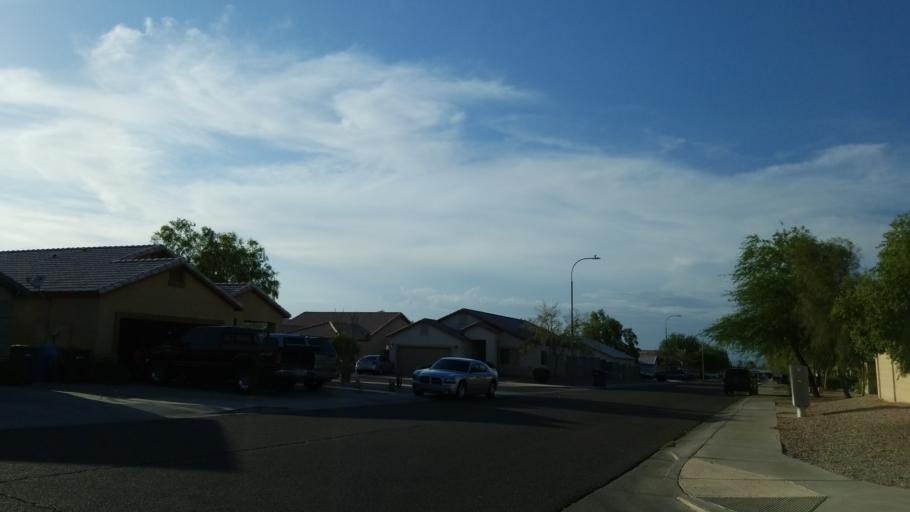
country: US
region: Arizona
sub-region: Maricopa County
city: Phoenix
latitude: 33.3927
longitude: -112.0867
